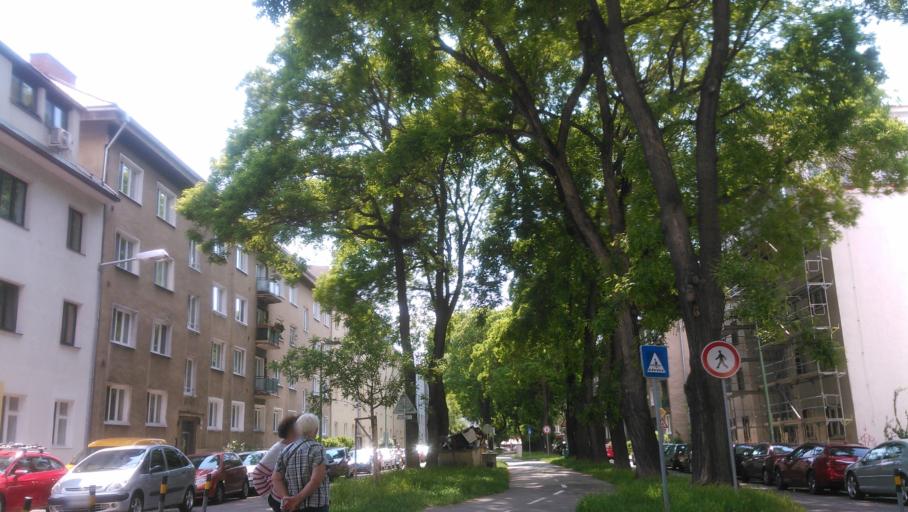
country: SK
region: Bratislavsky
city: Bratislava
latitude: 48.1507
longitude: 17.1379
